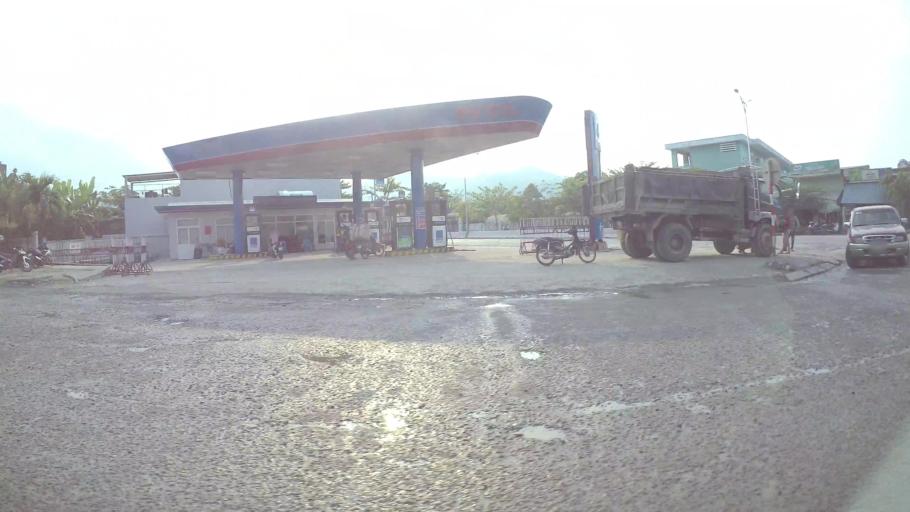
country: VN
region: Da Nang
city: Lien Chieu
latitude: 16.0513
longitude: 108.1511
